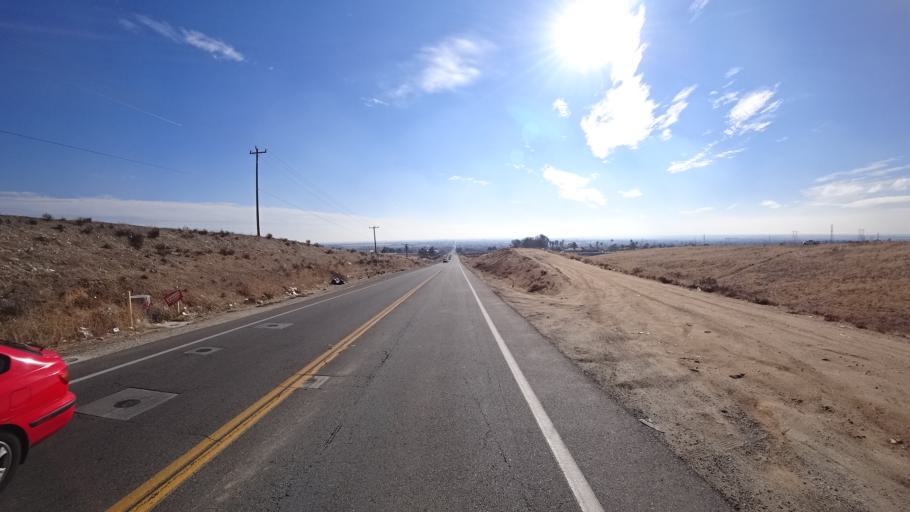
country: US
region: California
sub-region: Kern County
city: Bakersfield
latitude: 35.3876
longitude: -118.9145
